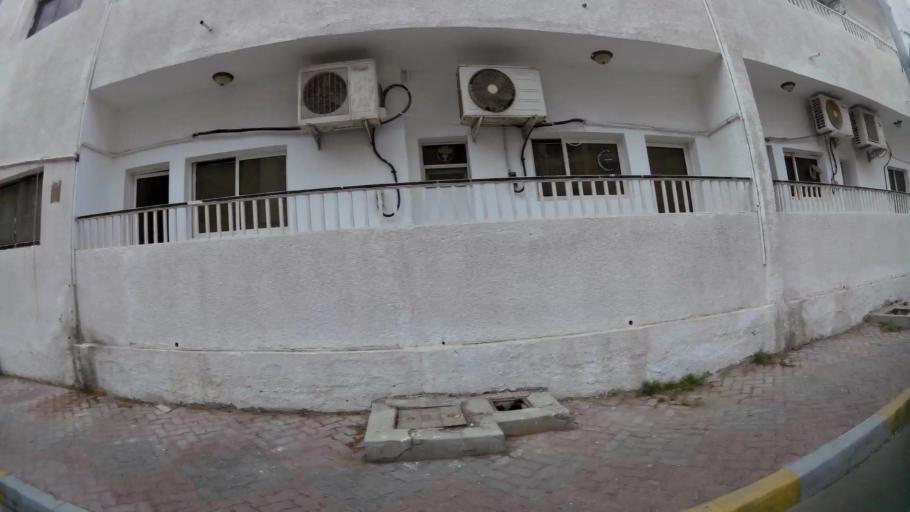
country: AE
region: Abu Dhabi
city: Abu Dhabi
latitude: 24.4458
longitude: 54.3985
